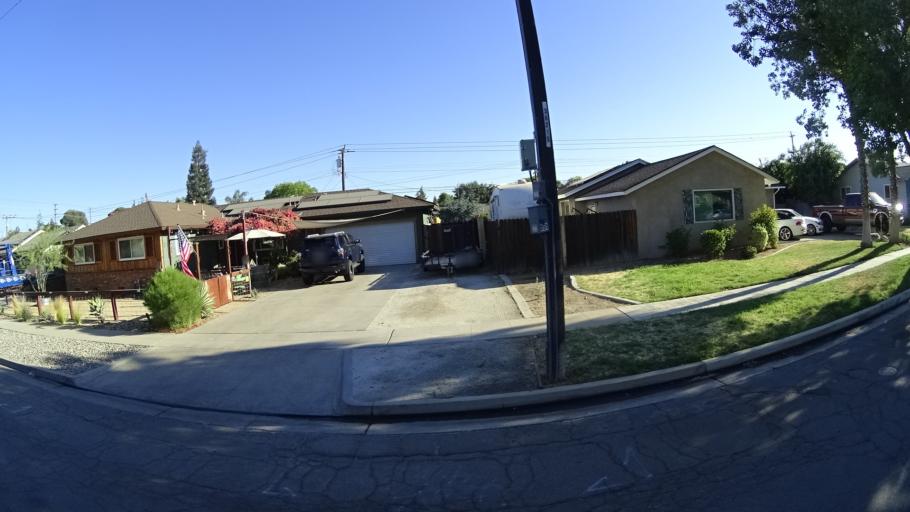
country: US
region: California
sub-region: Fresno County
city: Fresno
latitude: 36.8003
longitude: -119.8253
